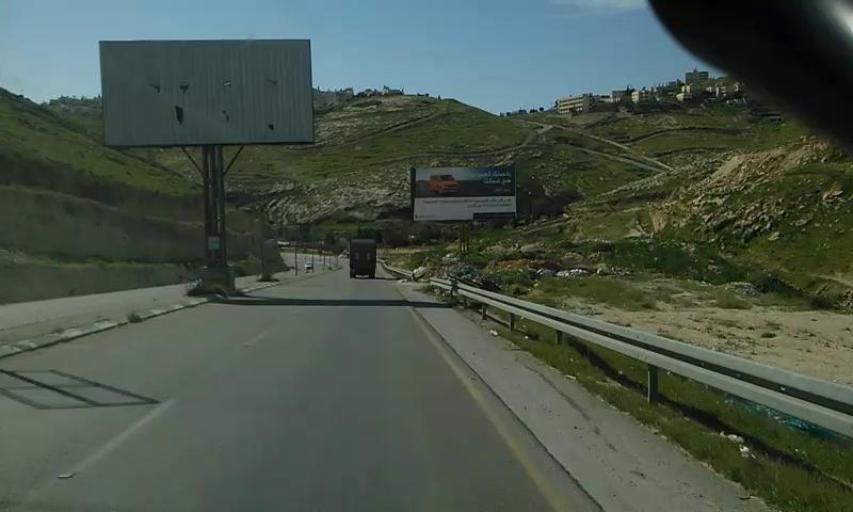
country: PS
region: West Bank
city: Abu Dis
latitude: 31.7469
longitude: 35.2805
